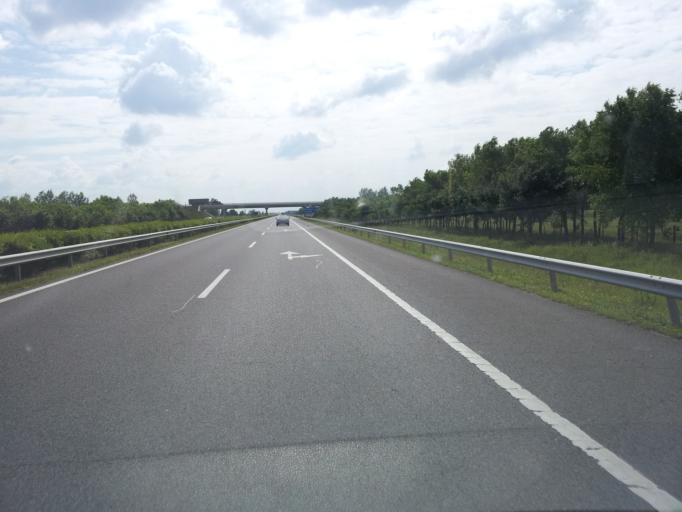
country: HU
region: Borsod-Abauj-Zemplen
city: Hejobaba
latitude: 47.8808
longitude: 20.8952
